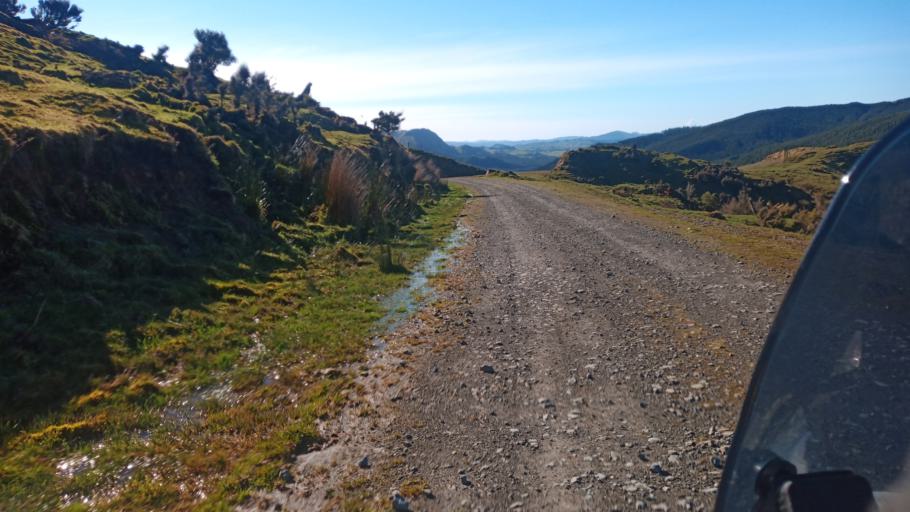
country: NZ
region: Gisborne
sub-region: Gisborne District
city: Gisborne
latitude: -38.1497
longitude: 177.8773
